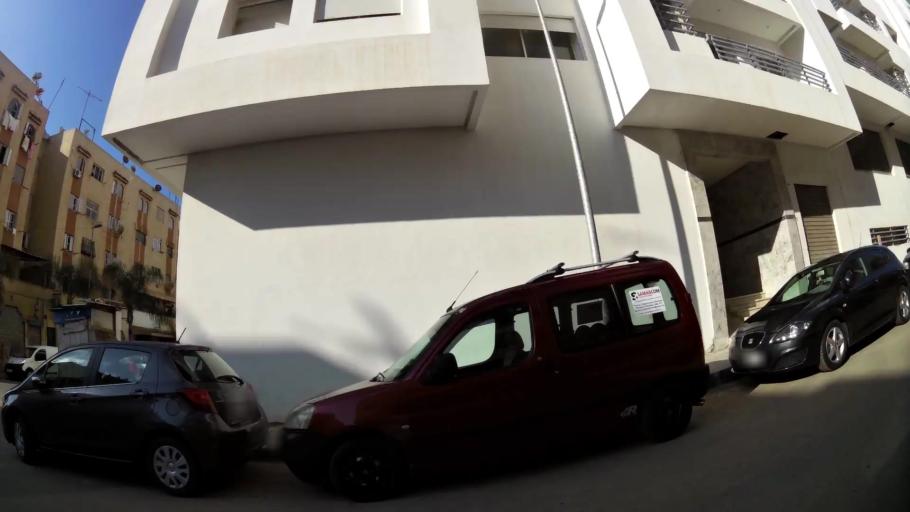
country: MA
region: Rabat-Sale-Zemmour-Zaer
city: Sale
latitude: 34.0500
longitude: -6.8005
